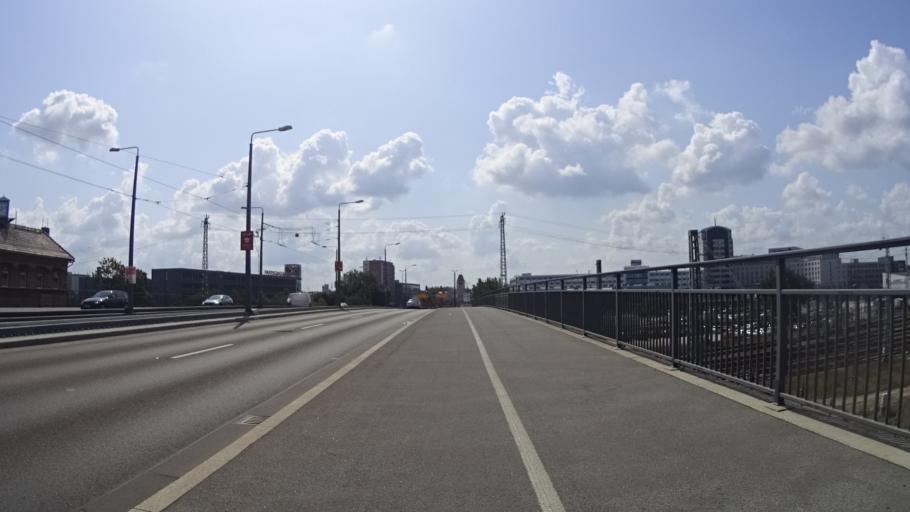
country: DE
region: Brandenburg
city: Cottbus
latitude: 51.7518
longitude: 14.3283
